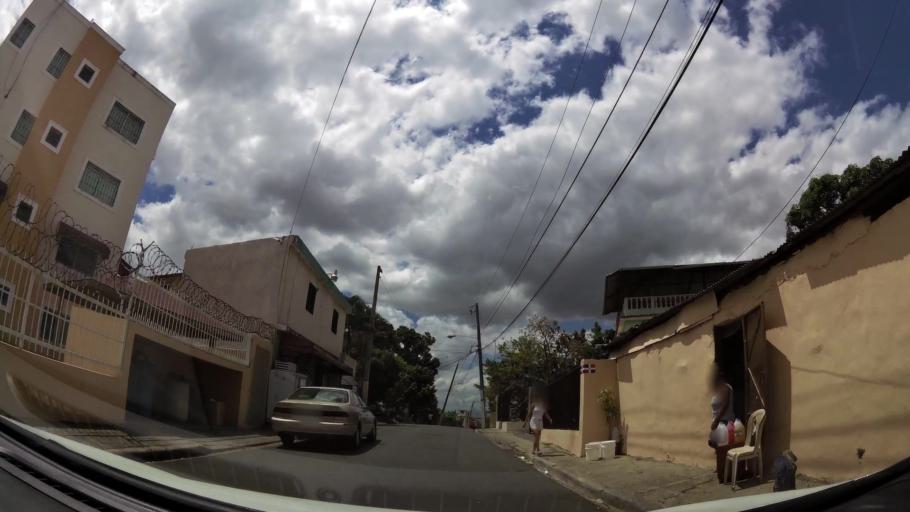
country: DO
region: Nacional
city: Ensanche Luperon
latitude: 18.5240
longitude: -69.9110
